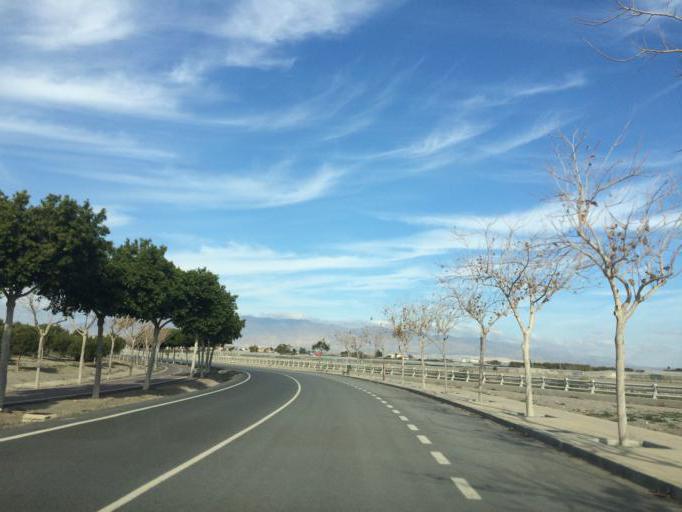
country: ES
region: Andalusia
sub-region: Provincia de Almeria
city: Almeria
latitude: 36.8282
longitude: -2.4282
